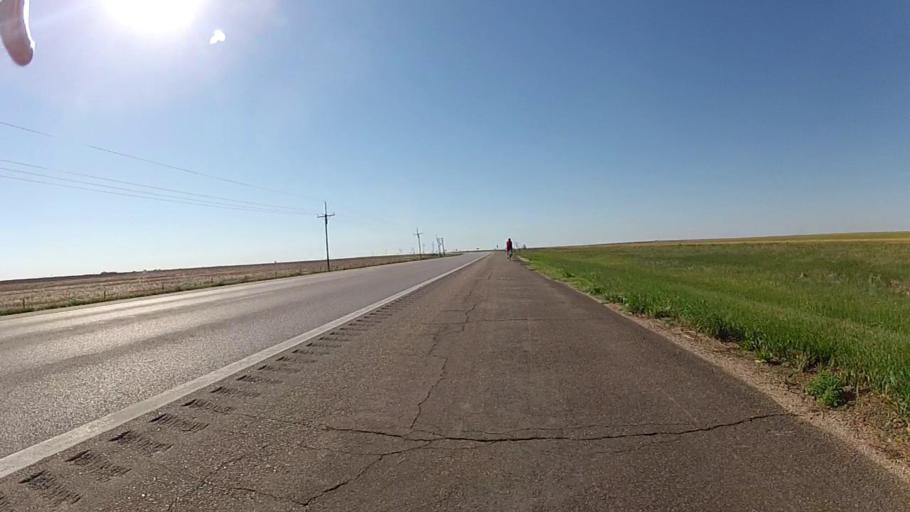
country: US
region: Kansas
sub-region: Ford County
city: Dodge City
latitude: 37.5900
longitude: -99.6879
